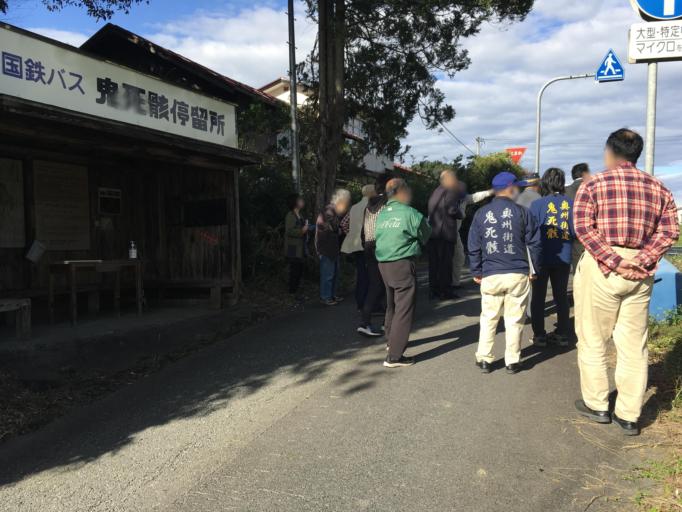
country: JP
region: Iwate
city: Ichinoseki
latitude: 38.7517
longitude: 141.0873
